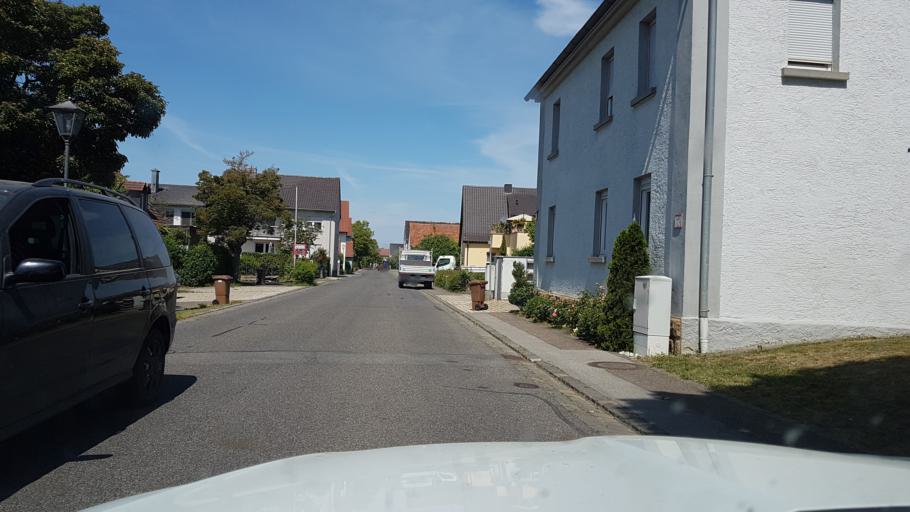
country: DE
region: Bavaria
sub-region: Regierungsbezirk Unterfranken
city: Hassfurt
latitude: 49.9964
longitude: 10.5039
